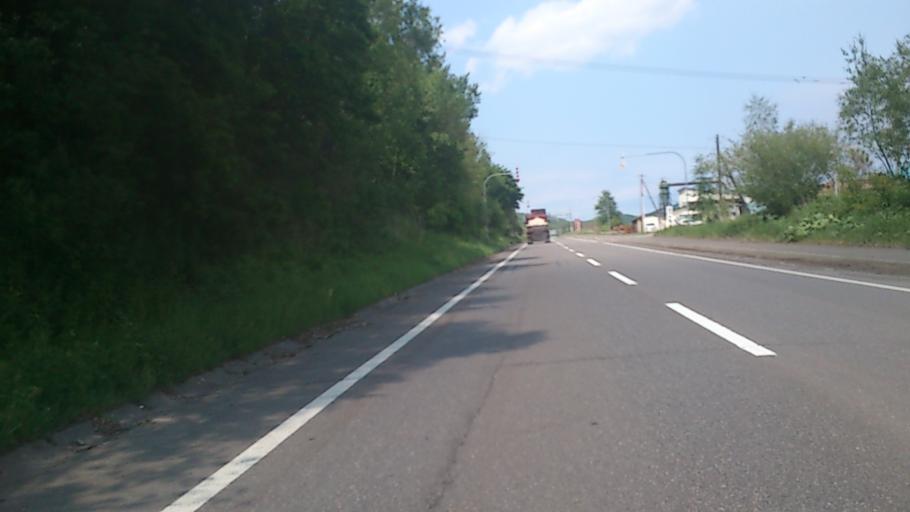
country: JP
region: Hokkaido
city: Otofuke
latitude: 43.2477
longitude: 143.5618
